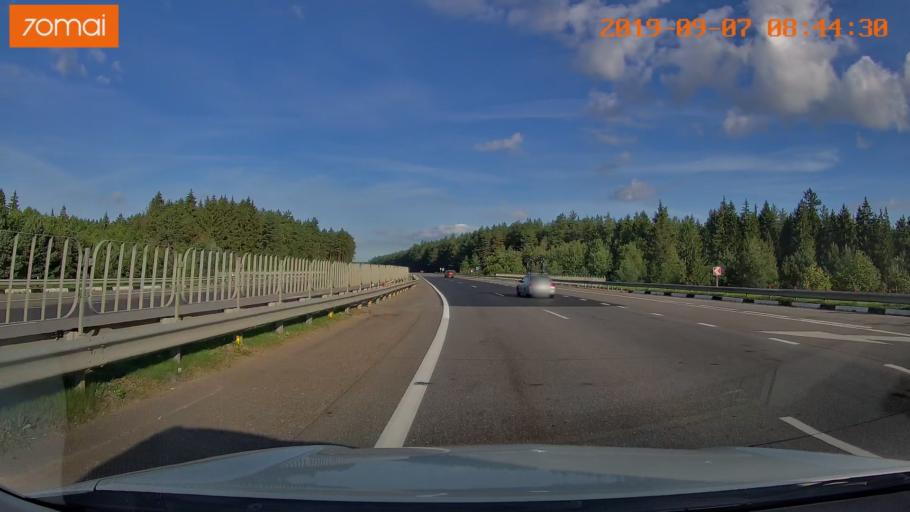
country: BY
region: Minsk
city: Rakaw
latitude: 53.9568
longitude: 27.1119
